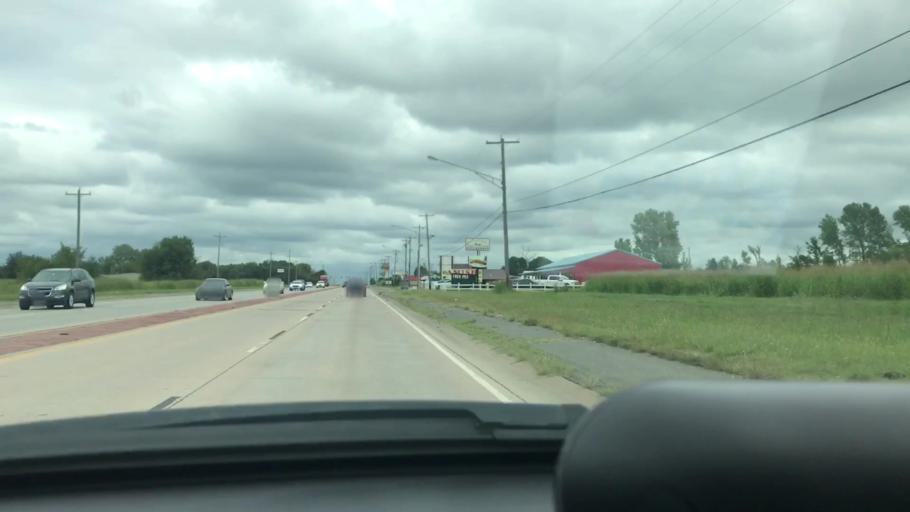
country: US
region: Oklahoma
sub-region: Muskogee County
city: Muskogee
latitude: 35.7780
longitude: -95.4024
